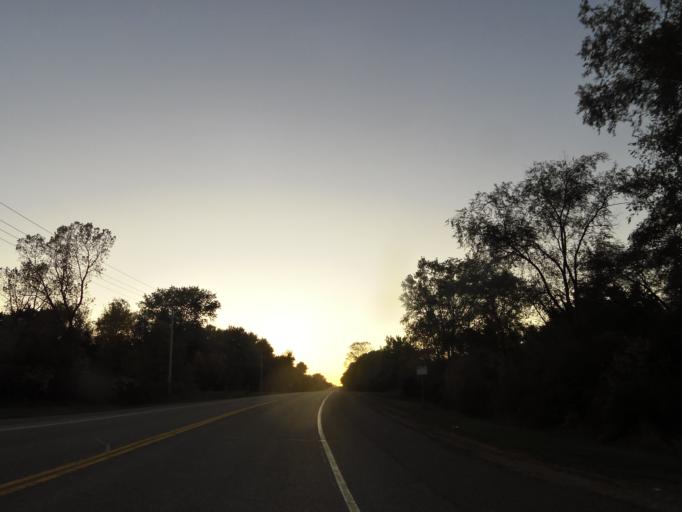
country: US
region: Minnesota
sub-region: Dakota County
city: Inver Grove Heights
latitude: 44.7901
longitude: -93.0713
